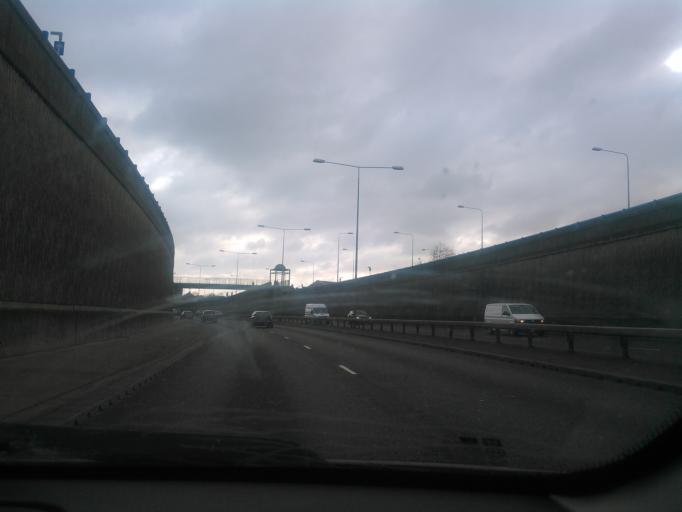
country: GB
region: England
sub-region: Staffordshire
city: Longton
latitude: 52.9870
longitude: -2.1389
